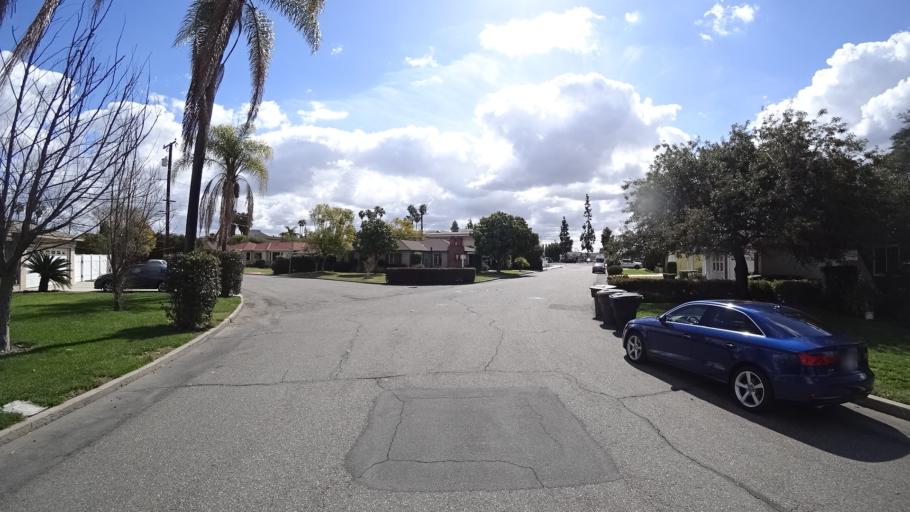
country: US
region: California
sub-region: Orange County
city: Anaheim
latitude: 33.8413
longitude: -117.8936
